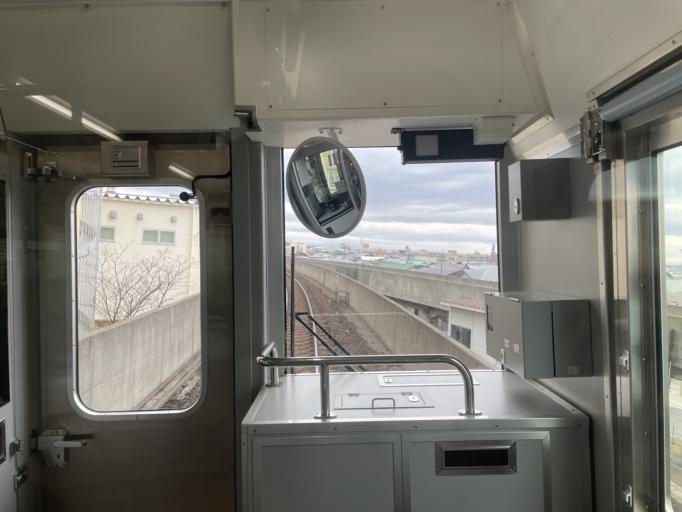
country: JP
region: Aomori
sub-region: Hachinohe Shi
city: Uchimaru
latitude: 40.5188
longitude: 141.5060
